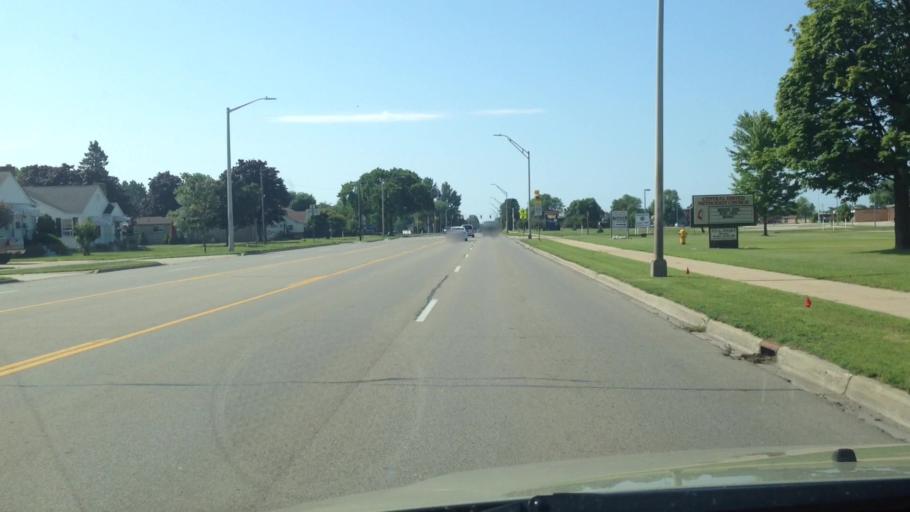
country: US
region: Michigan
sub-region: Delta County
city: Escanaba
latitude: 45.7432
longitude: -87.0799
